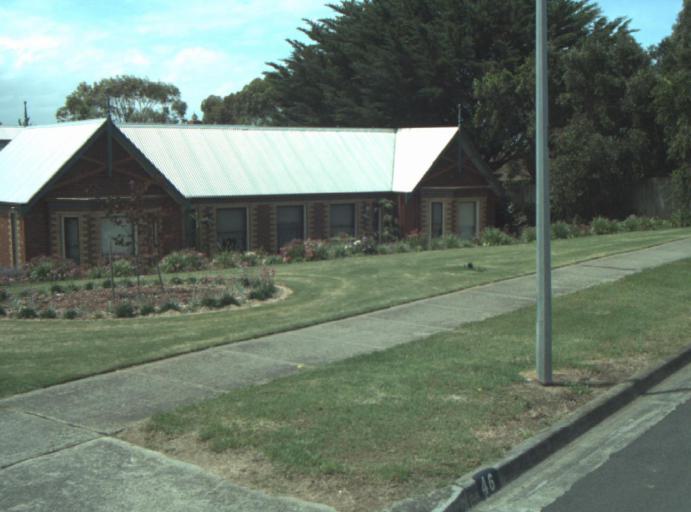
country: AU
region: Victoria
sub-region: Greater Geelong
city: Wandana Heights
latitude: -38.2034
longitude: 144.3174
